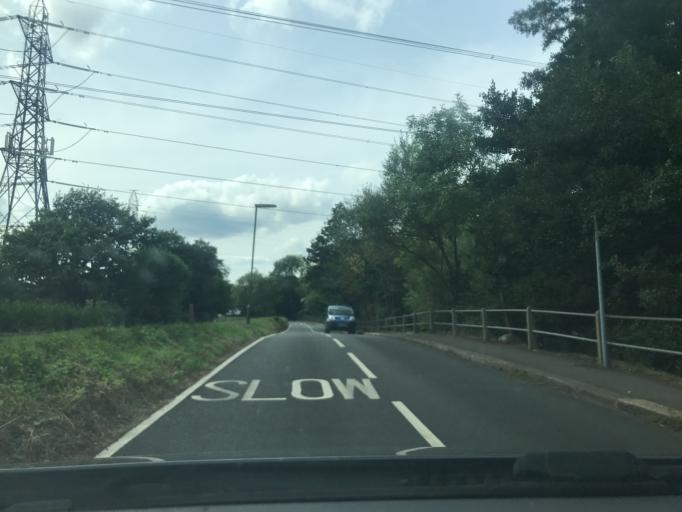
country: GB
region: England
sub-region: Surrey
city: Weybridge
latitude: 51.3718
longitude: -0.4681
